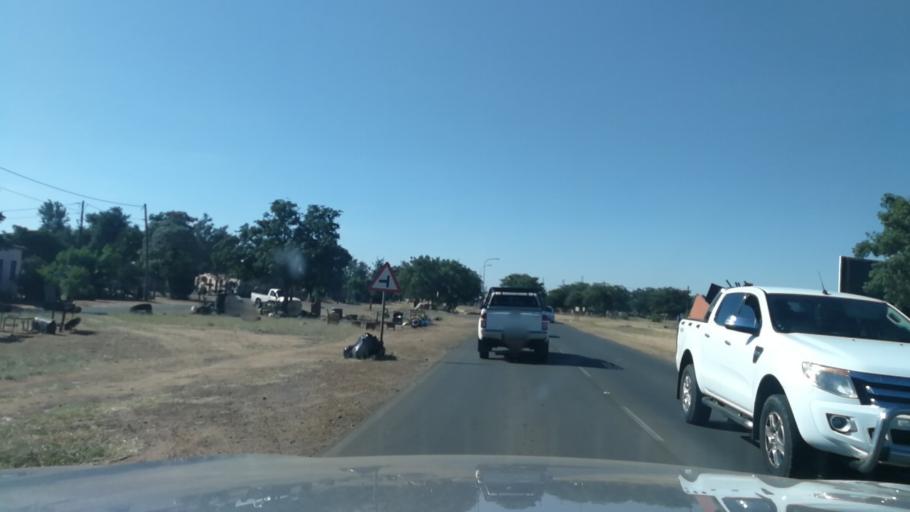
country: BW
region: South East
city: Gaborone
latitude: -24.6892
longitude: 25.9021
